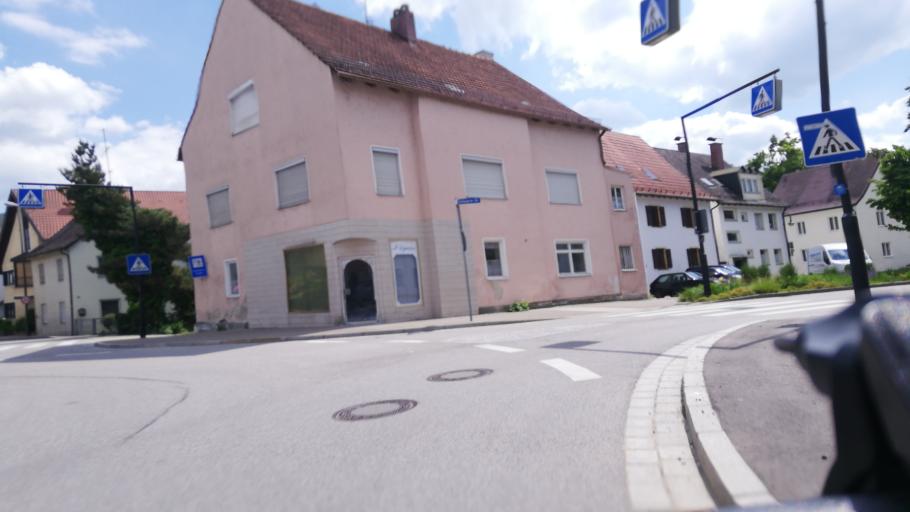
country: DE
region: Bavaria
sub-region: Upper Bavaria
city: Pfaffenhofen an der Ilm
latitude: 48.5289
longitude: 11.5042
